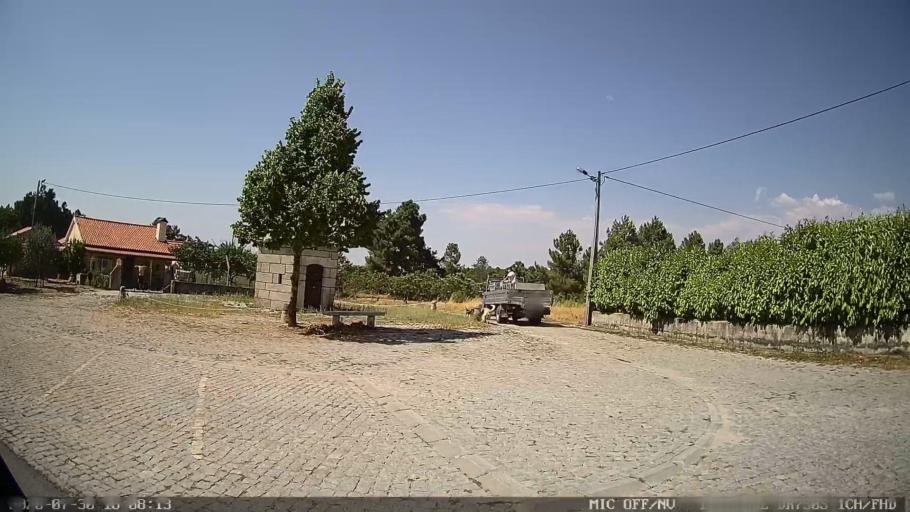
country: PT
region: Vila Real
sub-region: Murca
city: Murca
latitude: 41.3482
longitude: -7.4756
